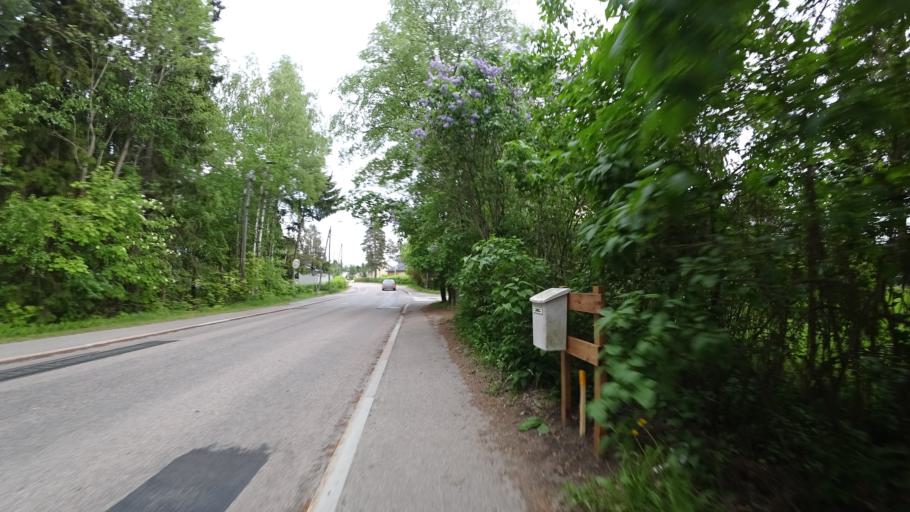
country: FI
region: Pirkanmaa
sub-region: Tampere
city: Yloejaervi
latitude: 61.5239
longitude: 23.6273
